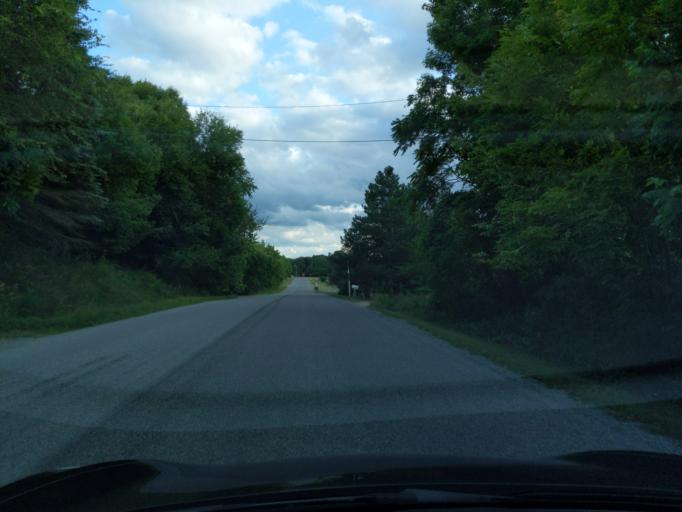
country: US
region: Michigan
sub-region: Ingham County
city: Holt
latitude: 42.6007
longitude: -84.5822
